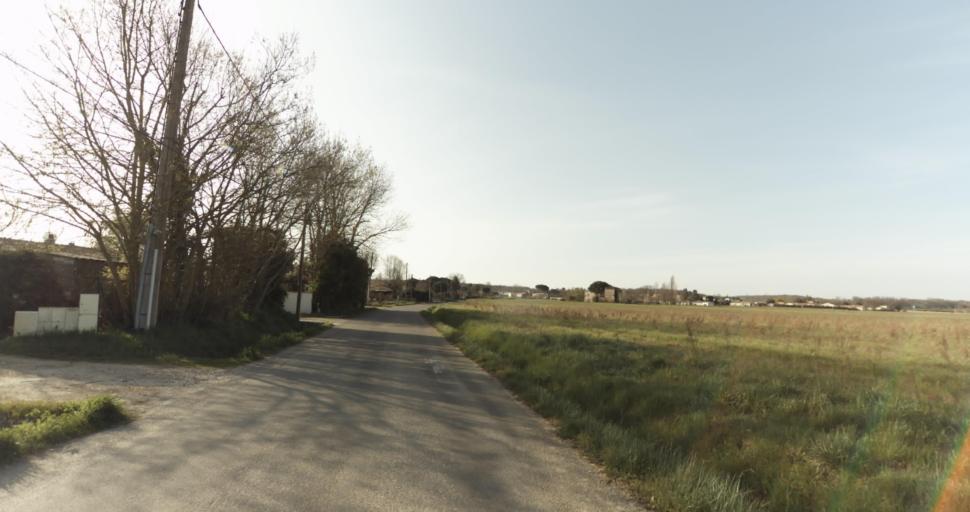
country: FR
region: Midi-Pyrenees
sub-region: Departement du Tarn
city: Saint-Sulpice-la-Pointe
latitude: 43.7626
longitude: 1.6775
